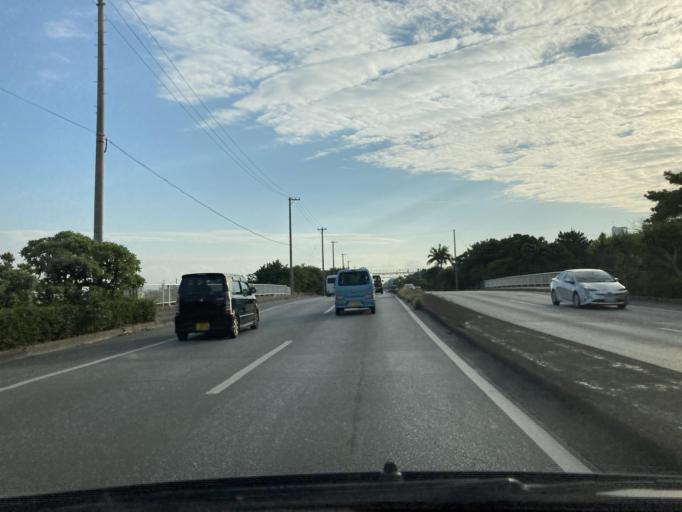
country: JP
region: Okinawa
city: Okinawa
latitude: 26.3266
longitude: 127.8349
